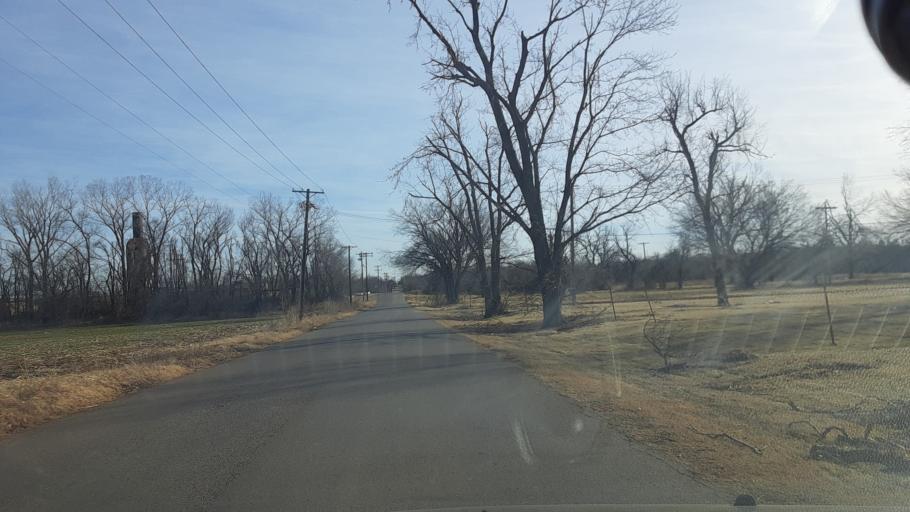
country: US
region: Oklahoma
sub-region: Logan County
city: Guthrie
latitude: 35.8853
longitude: -97.4322
